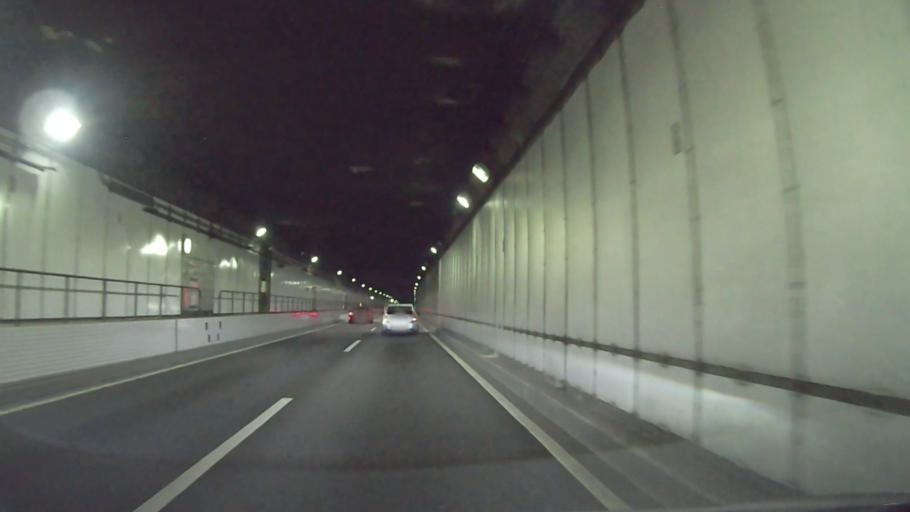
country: JP
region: Tokyo
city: Musashino
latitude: 35.7272
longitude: 139.6144
